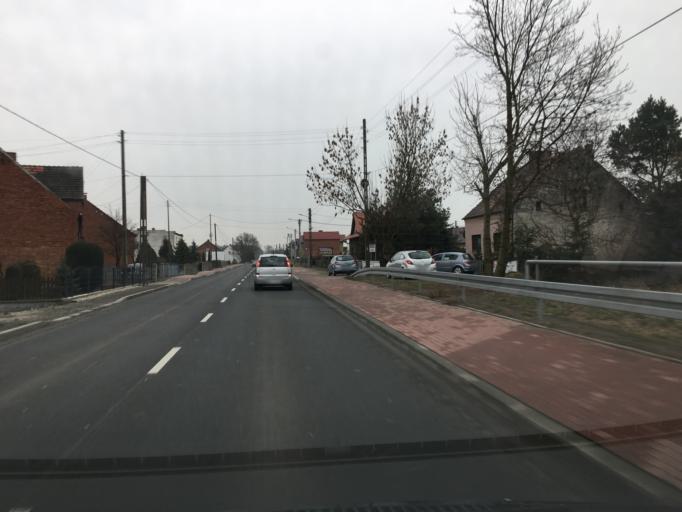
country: PL
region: Opole Voivodeship
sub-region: Powiat kedzierzynsko-kozielski
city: Bierawa
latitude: 50.3113
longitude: 18.2267
